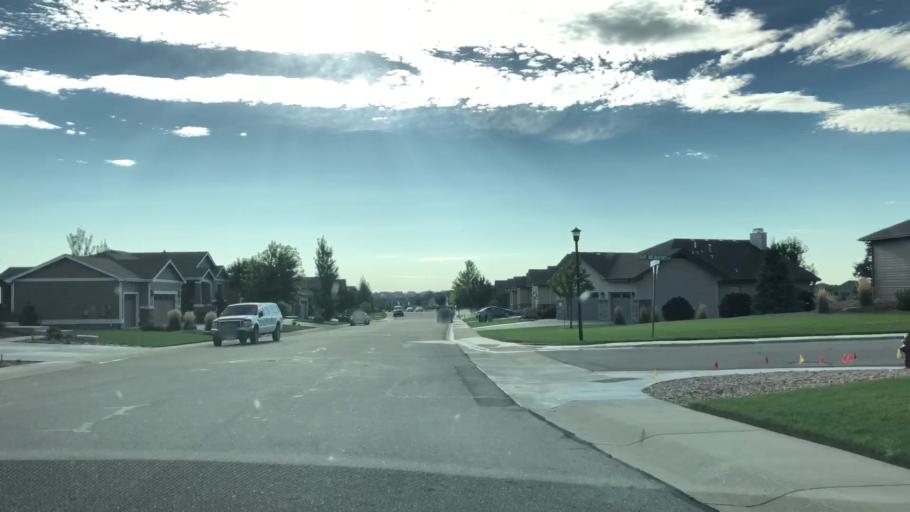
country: US
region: Colorado
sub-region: Weld County
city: Windsor
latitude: 40.4559
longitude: -104.9727
